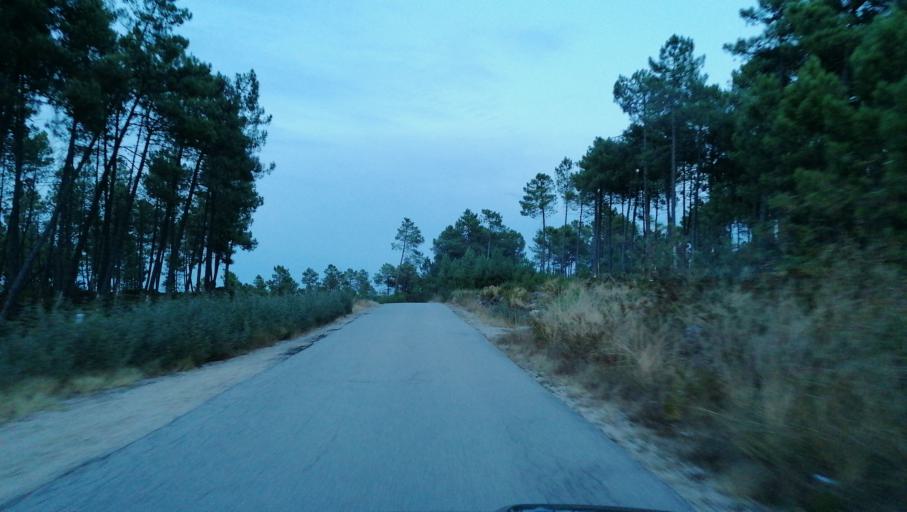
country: PT
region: Vila Real
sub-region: Vila Pouca de Aguiar
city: Vila Pouca de Aguiar
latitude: 41.5551
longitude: -7.6323
